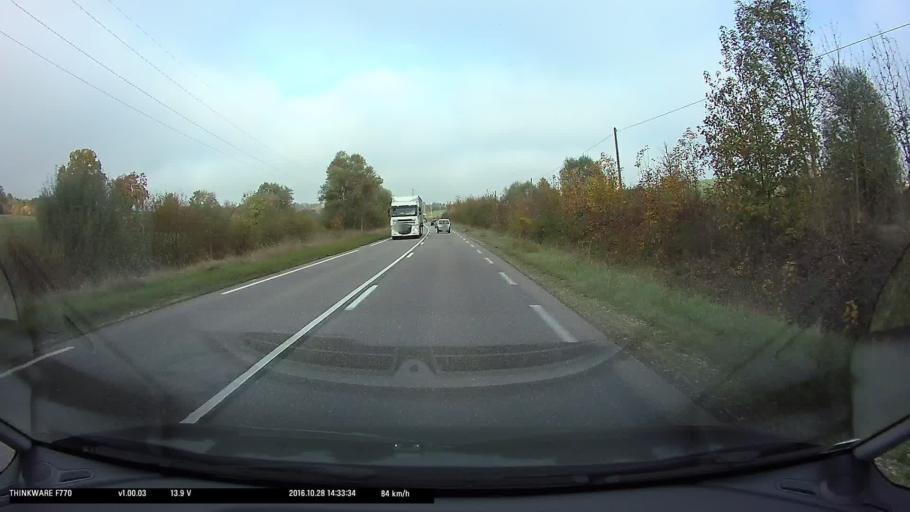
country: FR
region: Lorraine
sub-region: Departement de la Moselle
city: Lorquin
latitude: 48.6209
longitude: 6.8796
